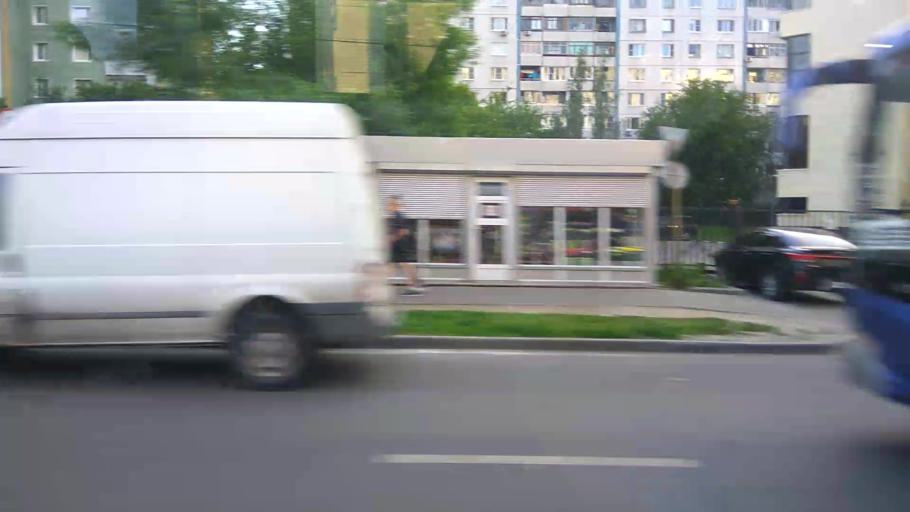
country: RU
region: Moskovskaya
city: Yubileyny
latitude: 55.9185
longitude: 37.8681
